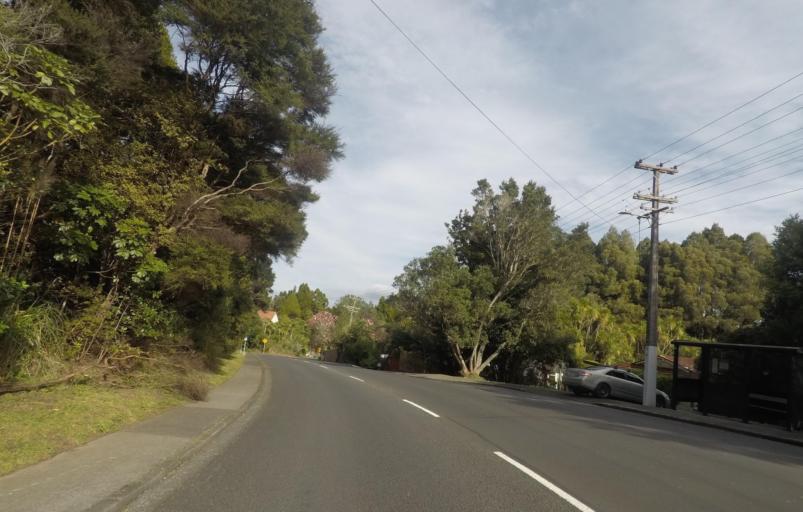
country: NZ
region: Auckland
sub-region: Auckland
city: Titirangi
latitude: -36.9389
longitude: 174.6381
